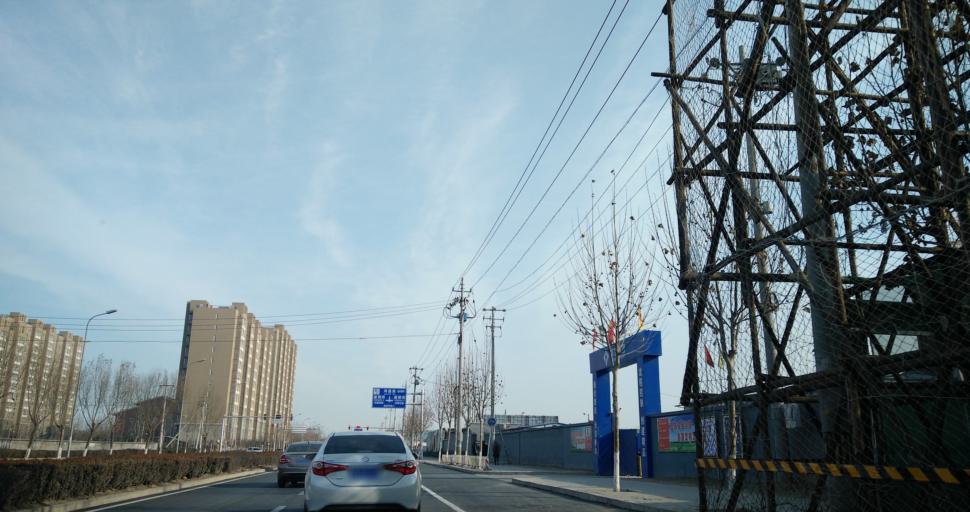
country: CN
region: Beijing
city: Xingfeng
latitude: 39.7083
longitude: 116.3962
